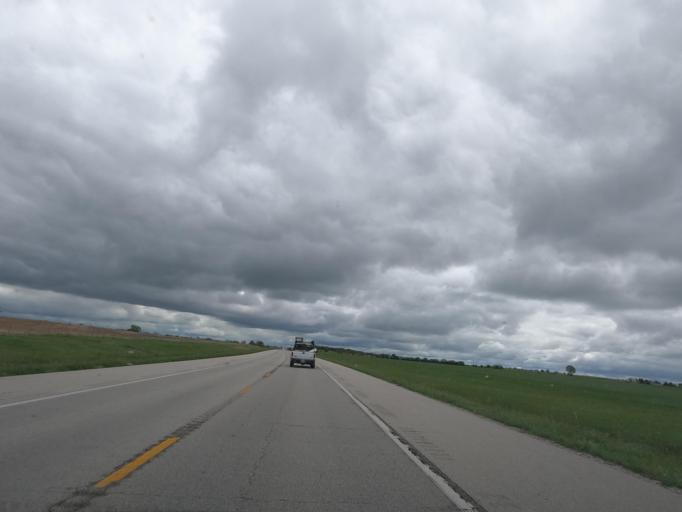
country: US
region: Kansas
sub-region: Wilson County
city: Fredonia
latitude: 37.5061
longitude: -95.7871
